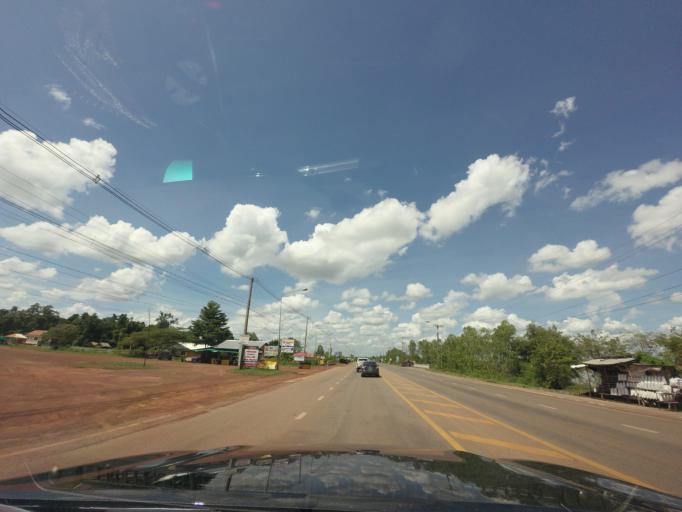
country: TH
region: Changwat Udon Thani
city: Ban Dung
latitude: 17.7127
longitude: 103.2502
